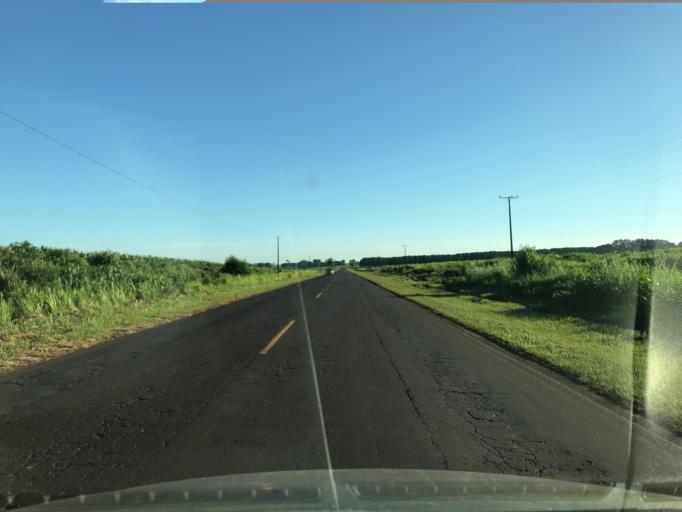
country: BR
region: Parana
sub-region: Ipora
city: Ipora
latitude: -24.1076
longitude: -53.8422
